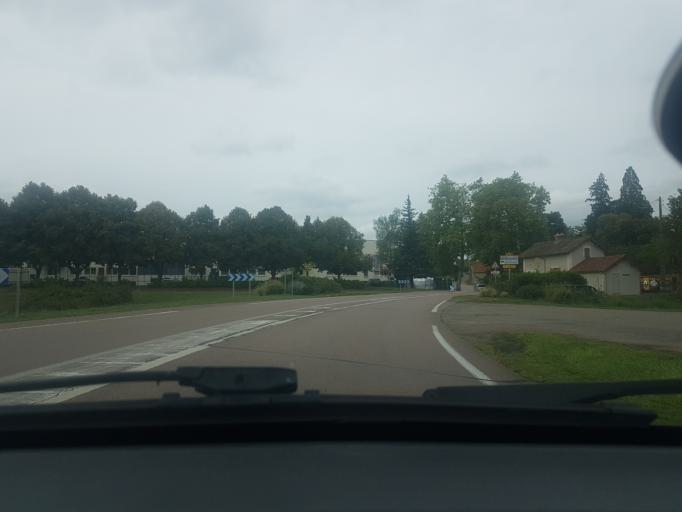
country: FR
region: Bourgogne
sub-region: Departement de la Cote-d'Or
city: Arnay-le-Duc
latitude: 47.1275
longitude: 4.4925
